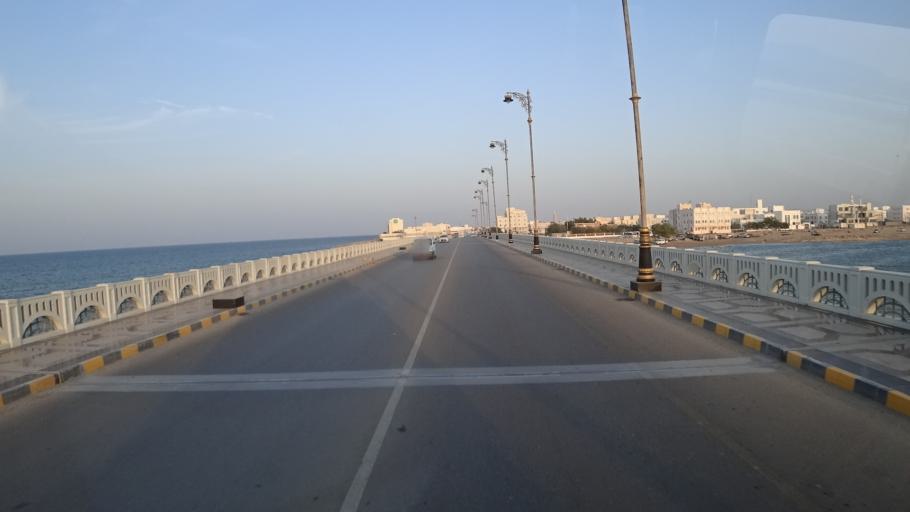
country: OM
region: Ash Sharqiyah
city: Sur
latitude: 22.5970
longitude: 59.4898
